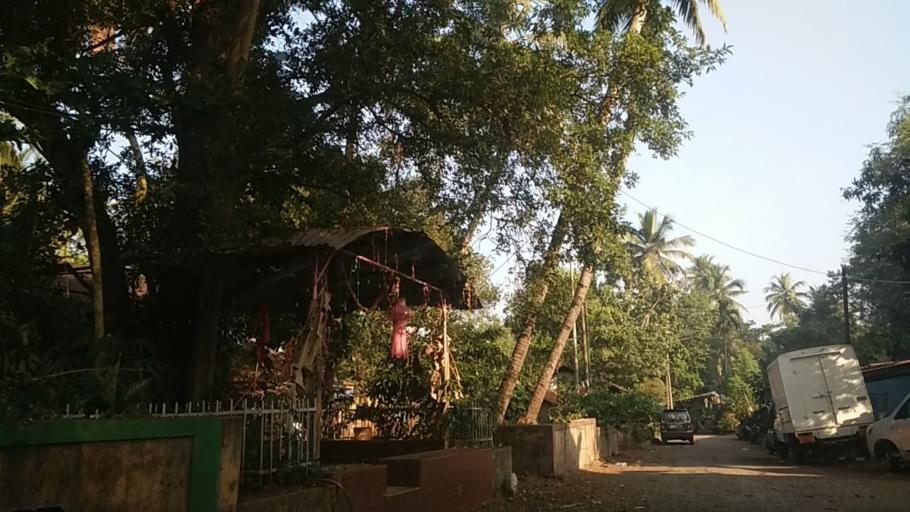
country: IN
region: Goa
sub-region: South Goa
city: Madgaon
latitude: 15.2777
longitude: 73.9538
